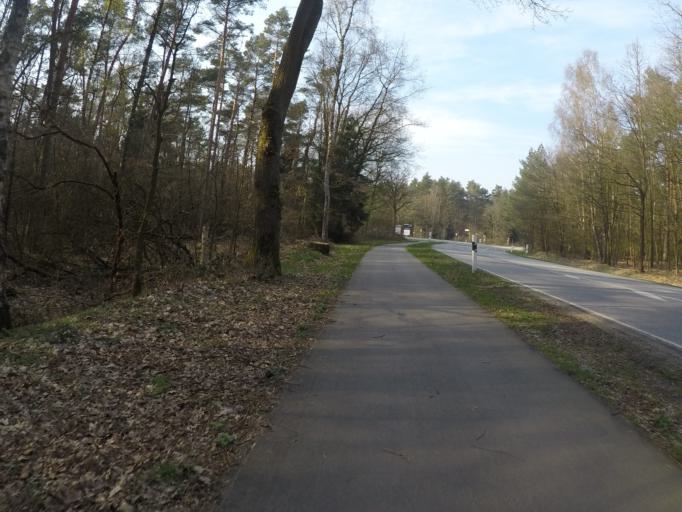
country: DE
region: Schleswig-Holstein
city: Wittenborn
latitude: 53.9457
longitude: 10.2205
